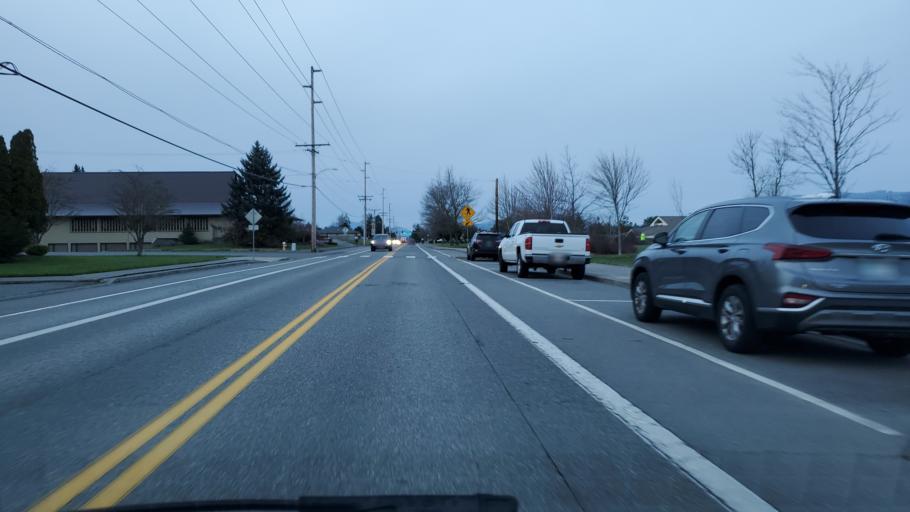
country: US
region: Washington
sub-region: Skagit County
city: Mount Vernon
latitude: 48.4178
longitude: -122.3188
